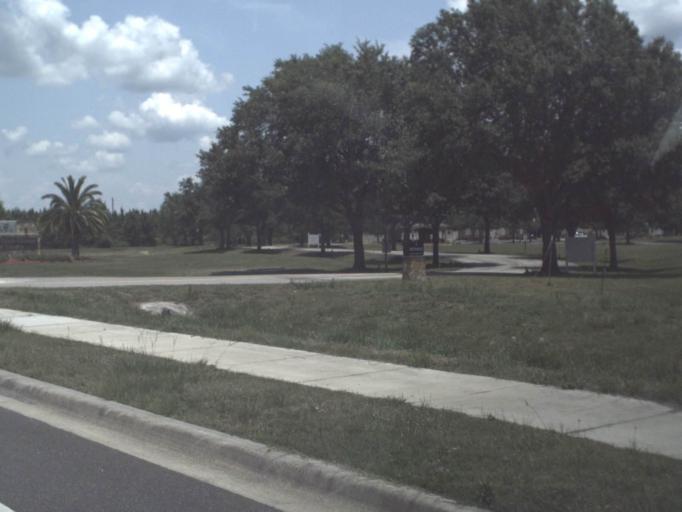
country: US
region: Florida
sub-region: Clay County
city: Green Cove Springs
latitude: 29.9719
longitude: -81.5046
